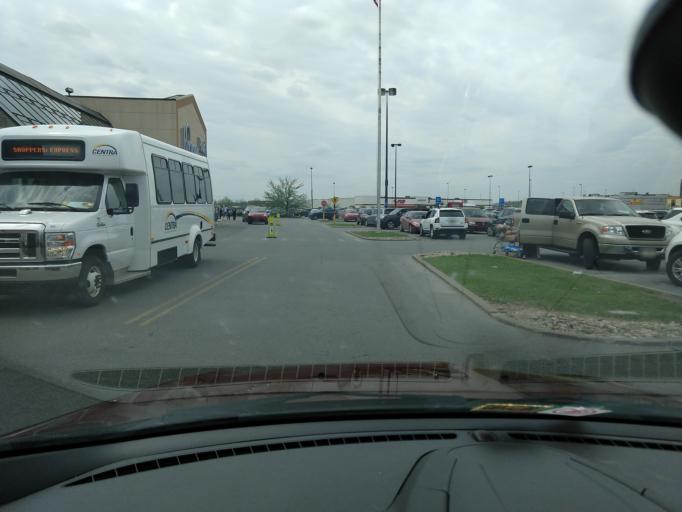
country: US
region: West Virginia
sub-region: Harrison County
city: Bridgeport
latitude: 39.2770
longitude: -80.2803
